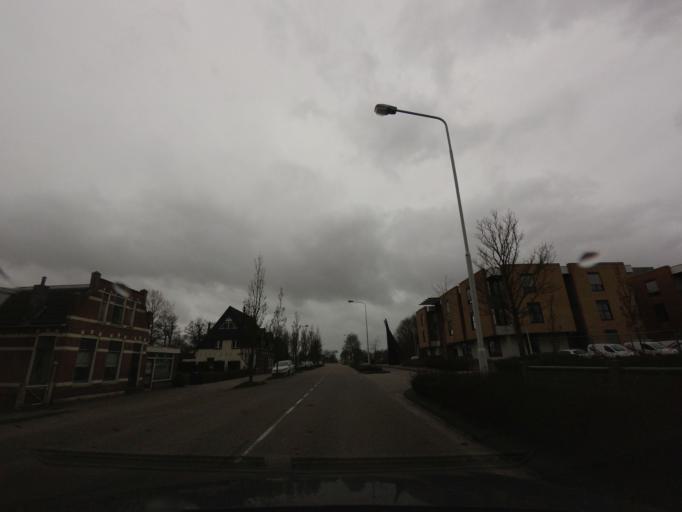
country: NL
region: Friesland
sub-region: Gemeente Franekeradeel
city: Franeker
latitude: 53.1843
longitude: 5.5353
